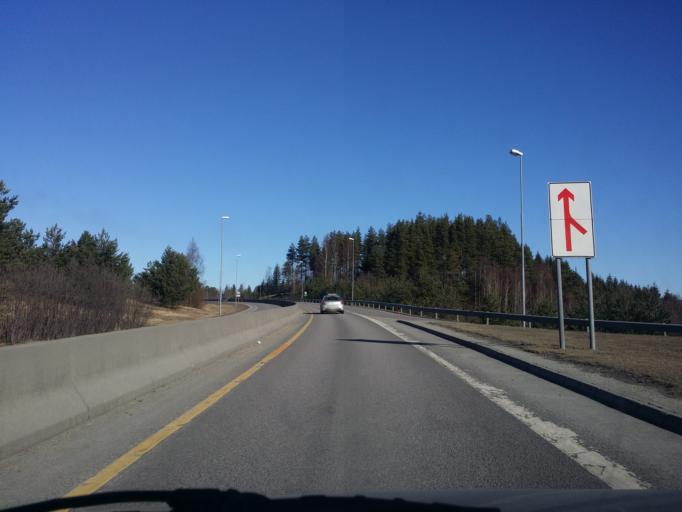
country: NO
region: Buskerud
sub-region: Ringerike
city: Honefoss
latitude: 60.2016
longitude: 10.2598
